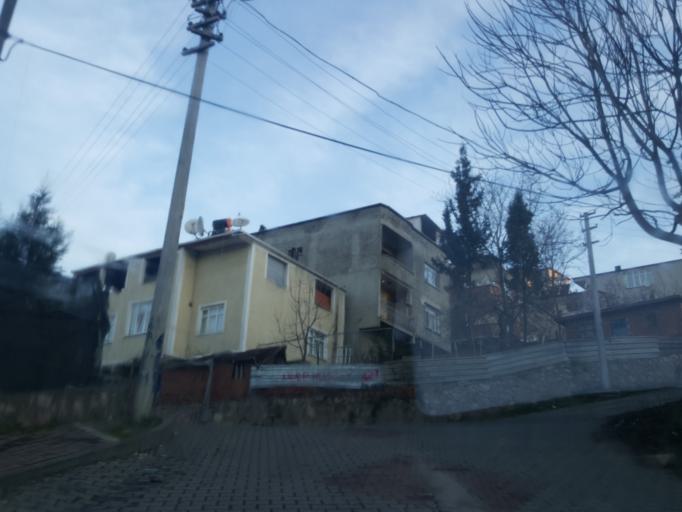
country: TR
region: Kocaeli
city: Tavsancil
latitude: 40.7860
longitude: 29.5460
